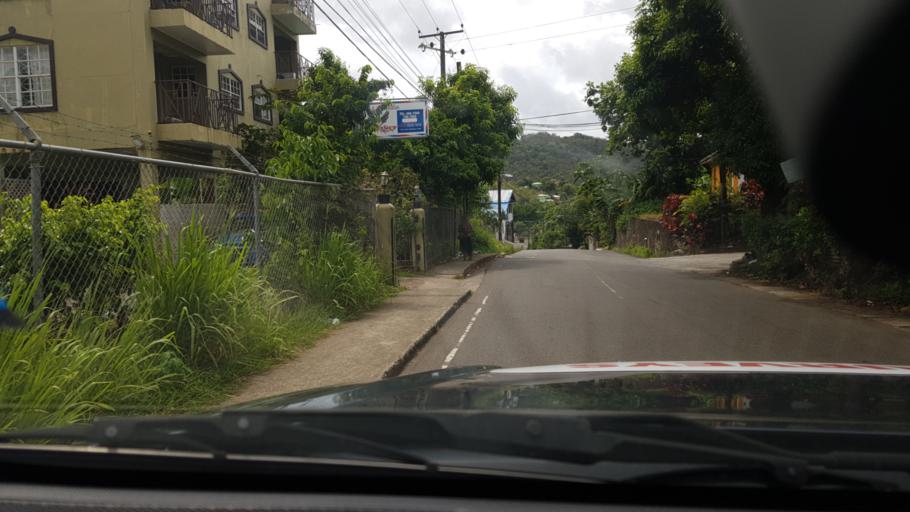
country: LC
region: Castries Quarter
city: Bisee
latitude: 14.0140
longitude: -60.9546
